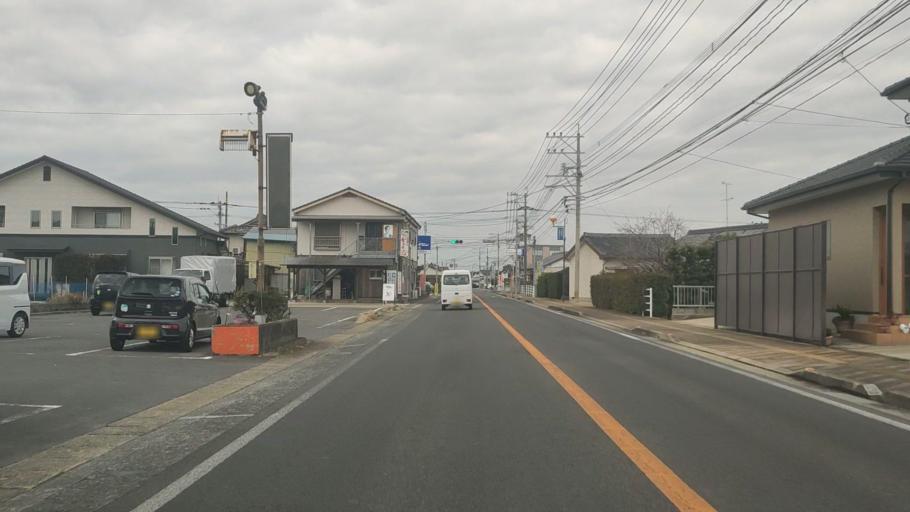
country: JP
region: Nagasaki
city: Shimabara
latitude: 32.8571
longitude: 130.3363
